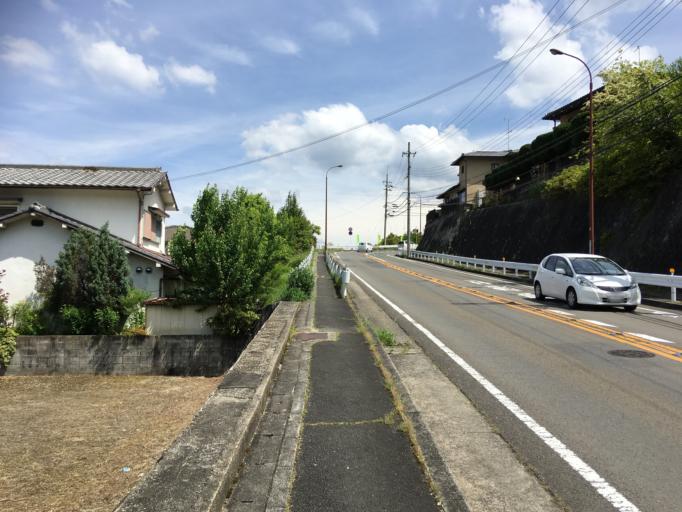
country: JP
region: Nara
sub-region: Ikoma-shi
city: Ikoma
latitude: 34.7129
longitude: 135.7131
